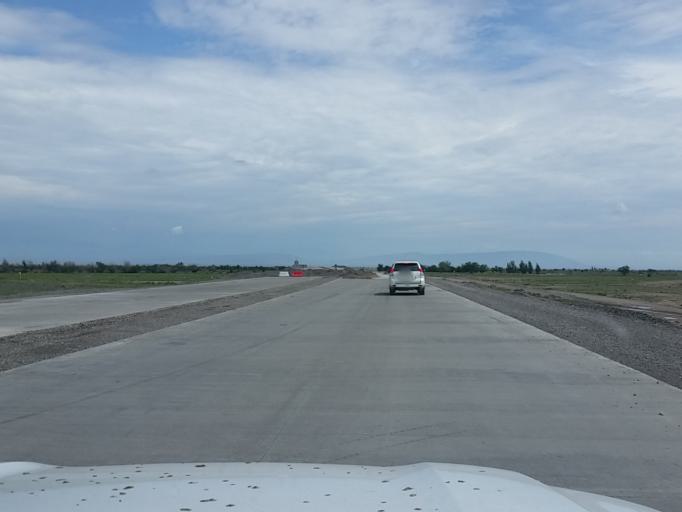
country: KZ
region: Almaty Oblysy
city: Turgen'
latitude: 43.6269
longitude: 78.3729
